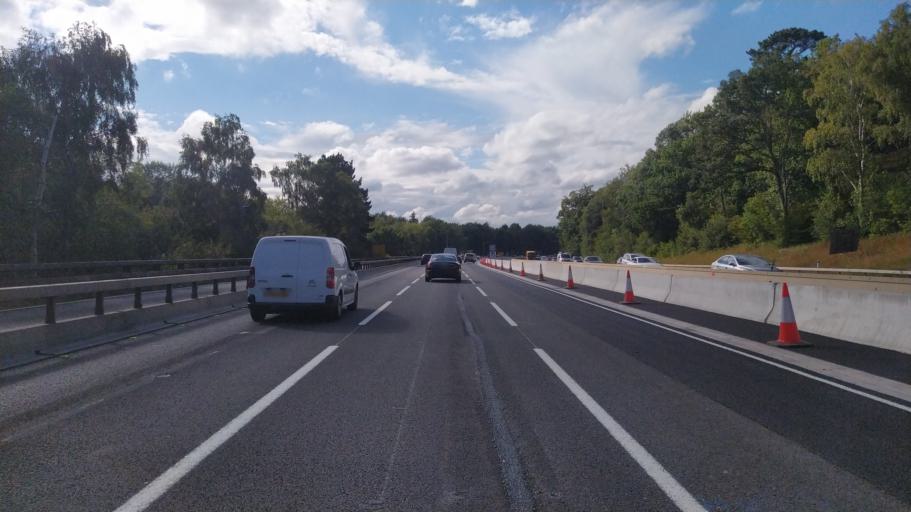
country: GB
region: England
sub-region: Hampshire
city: Botley
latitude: 50.8807
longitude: -1.2795
